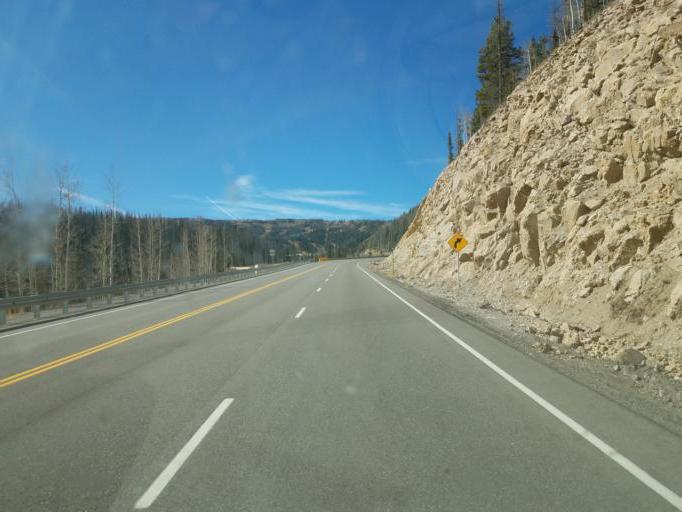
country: US
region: Colorado
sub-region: Archuleta County
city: Pagosa Springs
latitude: 37.4795
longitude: -106.7736
